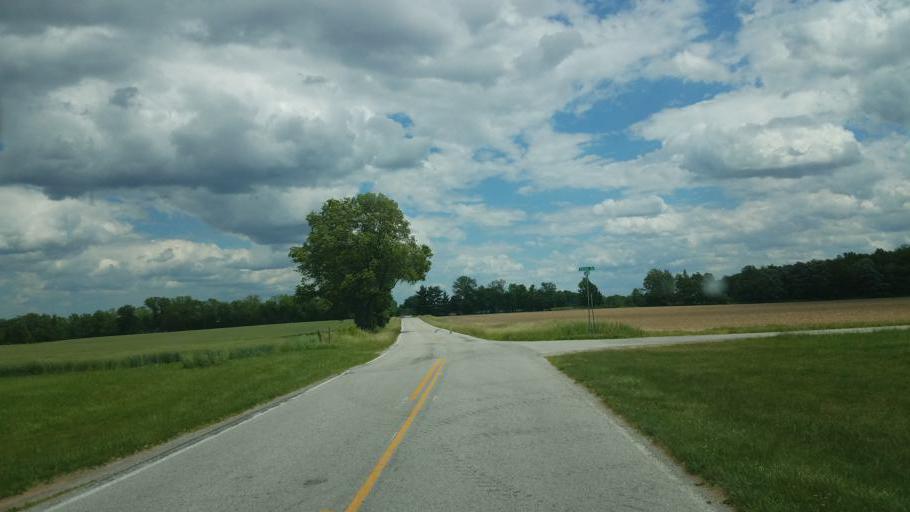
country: US
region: Ohio
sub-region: Huron County
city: Monroeville
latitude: 41.1820
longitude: -82.7483
